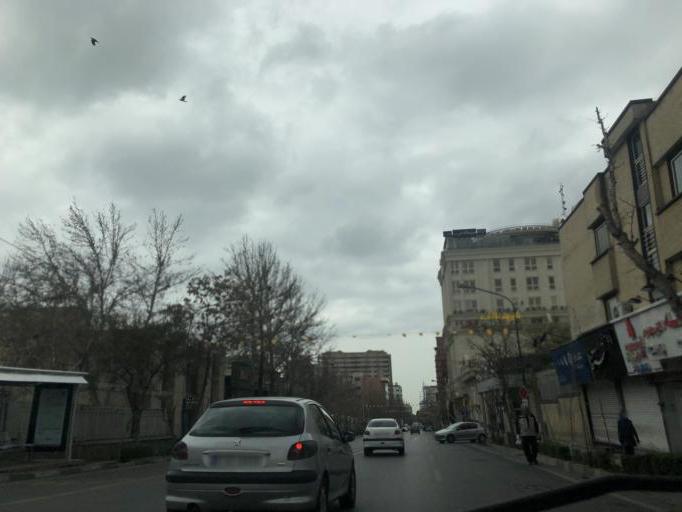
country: IR
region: Tehran
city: Tajrish
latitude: 35.7777
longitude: 51.4663
